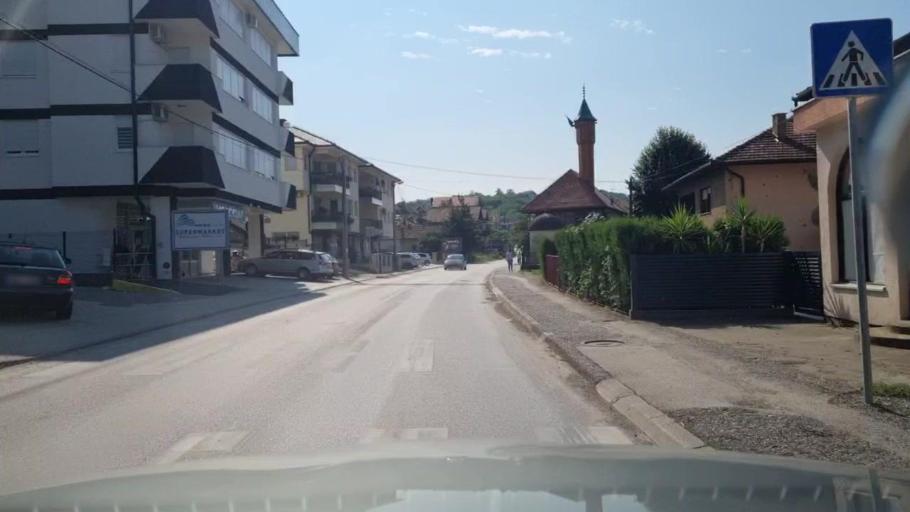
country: BA
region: Federation of Bosnia and Herzegovina
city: Gradacac
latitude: 44.8770
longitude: 18.4323
